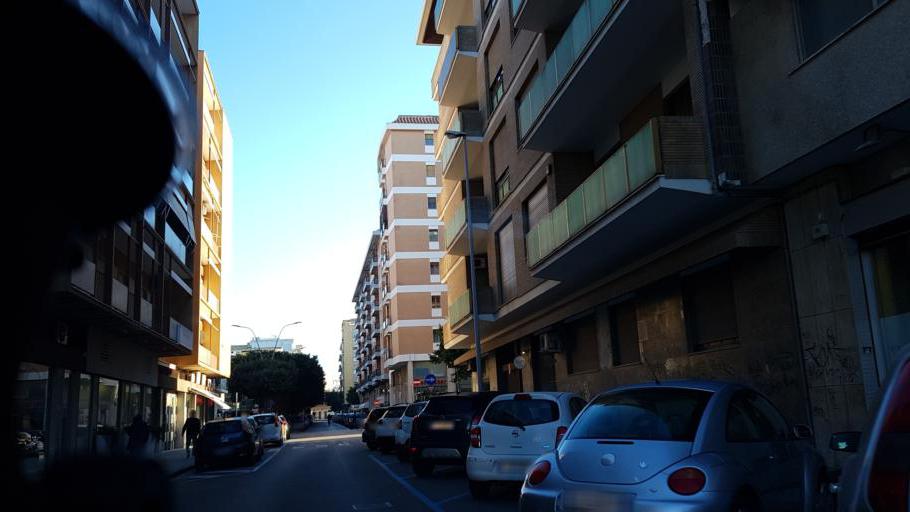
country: IT
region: Apulia
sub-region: Provincia di Lecce
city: Lecce
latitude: 40.3546
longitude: 18.1810
